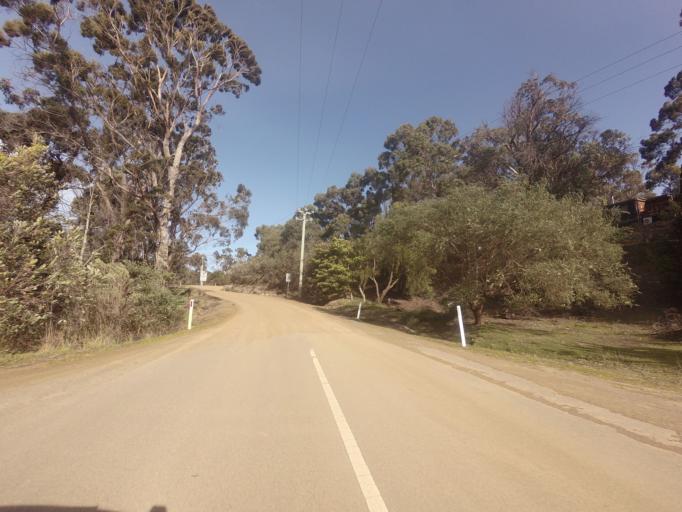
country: AU
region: Tasmania
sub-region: Kingborough
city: Margate
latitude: -43.0780
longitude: 147.2652
